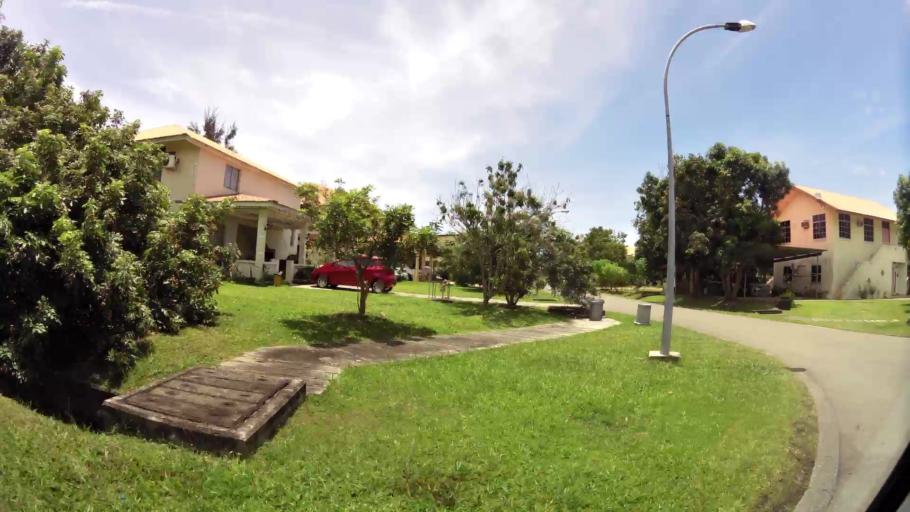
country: BN
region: Belait
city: Kuala Belait
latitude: 4.5900
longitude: 114.2460
